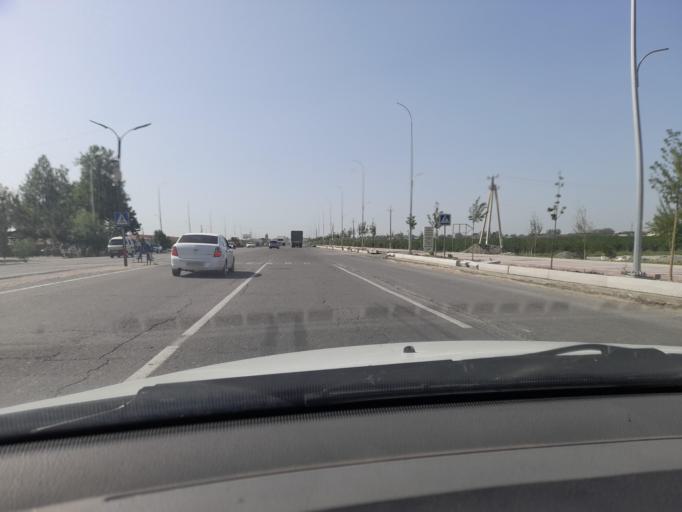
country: UZ
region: Samarqand
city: Daxbet
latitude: 39.7340
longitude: 66.9341
